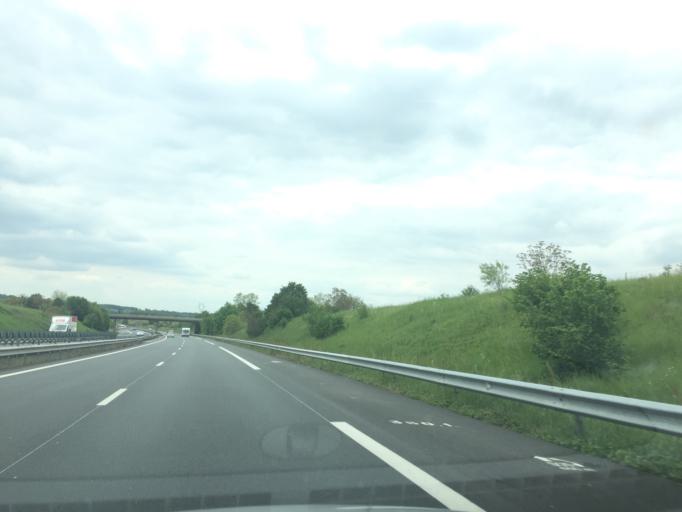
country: FR
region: Poitou-Charentes
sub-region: Departement des Deux-Sevres
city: La Creche
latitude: 46.3633
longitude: -0.2618
